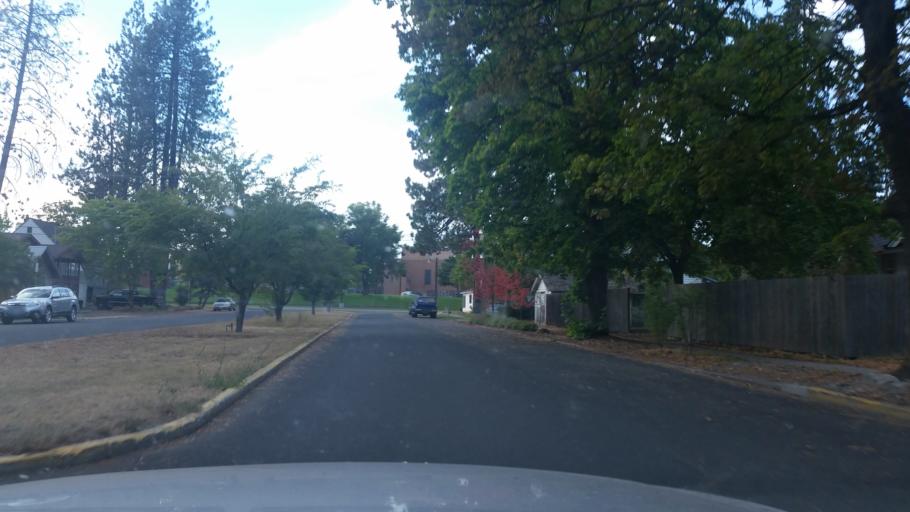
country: US
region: Washington
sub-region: Spokane County
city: Cheney
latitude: 47.4866
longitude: -117.5837
